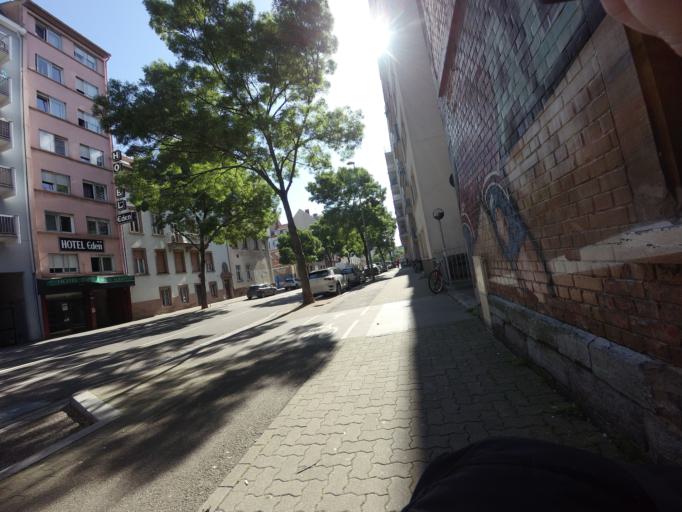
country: FR
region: Alsace
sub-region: Departement du Bas-Rhin
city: Strasbourg
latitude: 48.5783
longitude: 7.7318
